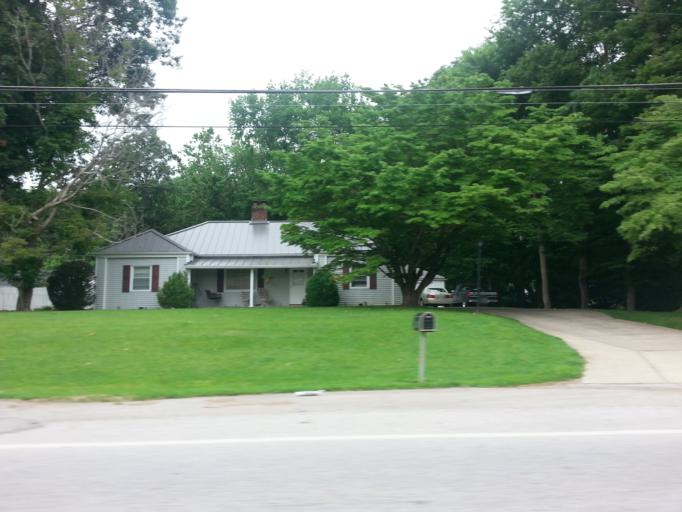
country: US
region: Ohio
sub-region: Brown County
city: Ripley
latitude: 38.7287
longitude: -83.8344
